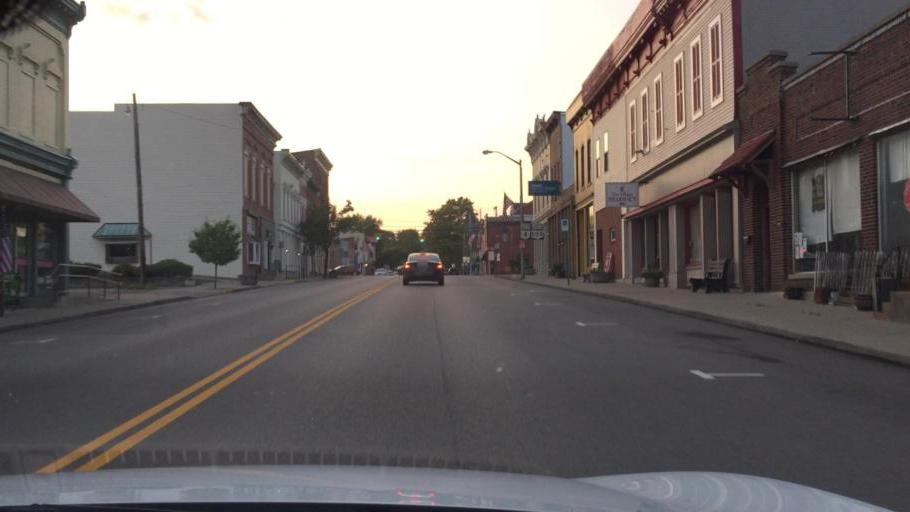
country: US
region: Ohio
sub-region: Champaign County
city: Mechanicsburg
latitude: 40.0713
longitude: -83.5551
